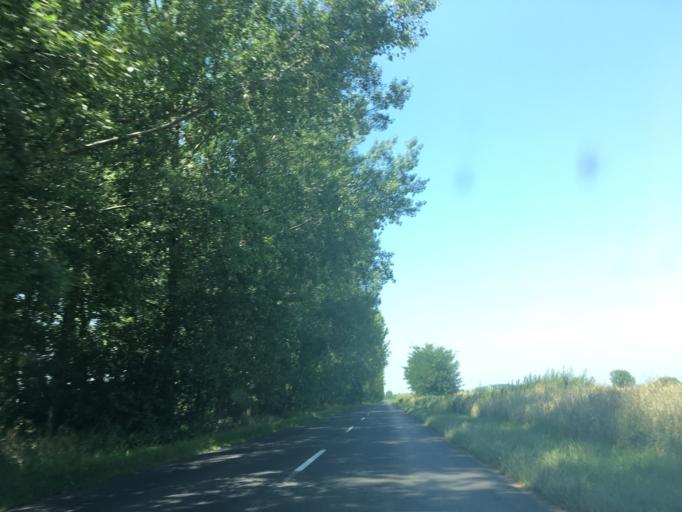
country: HU
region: Hajdu-Bihar
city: Mikepercs
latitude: 47.4781
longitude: 21.6504
